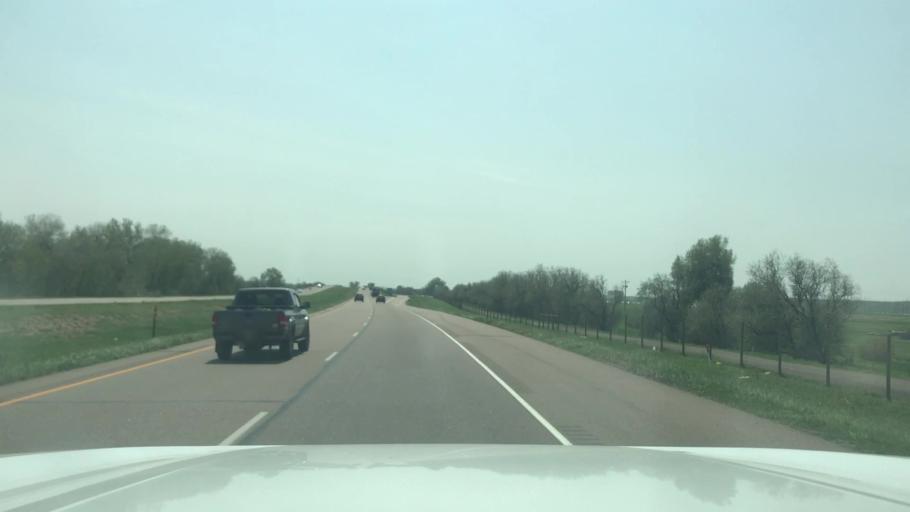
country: US
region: Colorado
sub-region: El Paso County
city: Fountain
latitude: 38.6151
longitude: -104.6870
